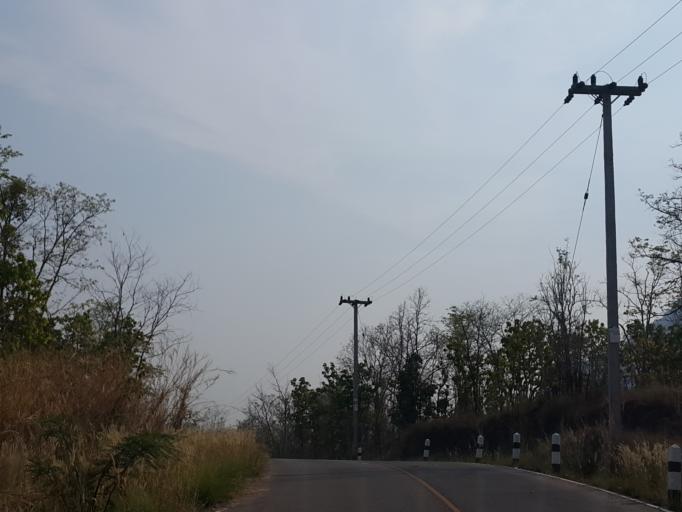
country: TH
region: Lampang
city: Chae Hom
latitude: 18.7379
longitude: 99.5465
